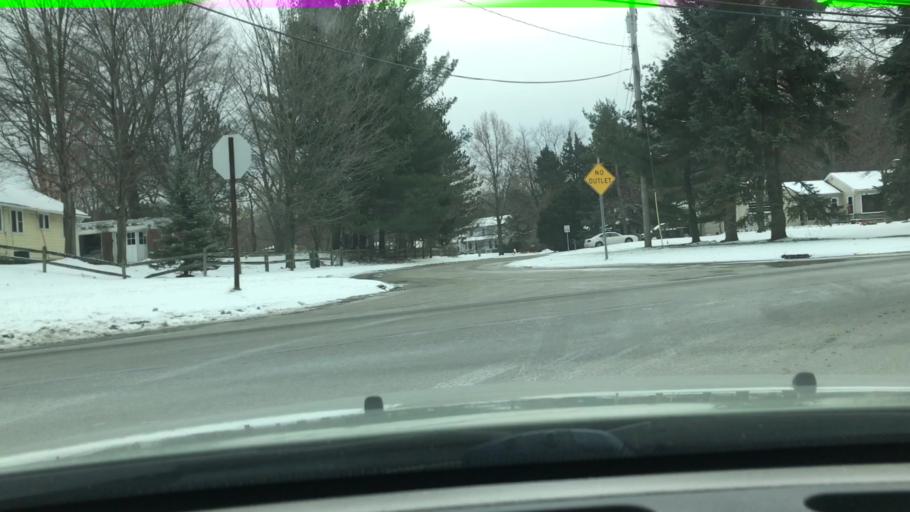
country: US
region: Ohio
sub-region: Lake County
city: Mentor
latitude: 41.6864
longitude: -81.3134
